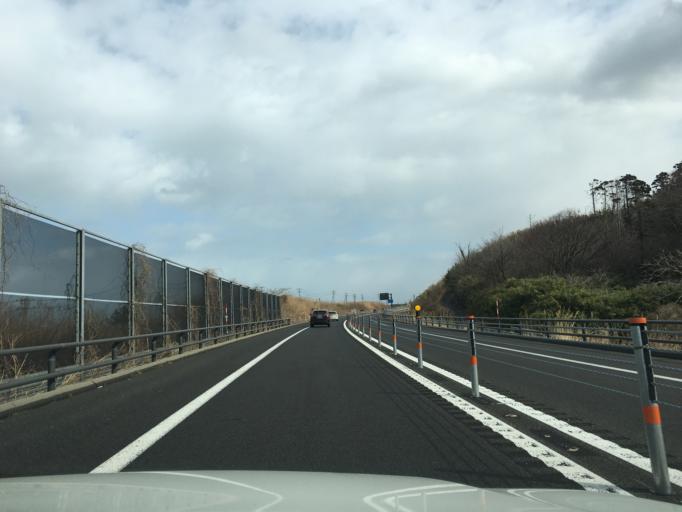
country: JP
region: Yamagata
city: Yuza
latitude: 39.3012
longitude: 139.9773
